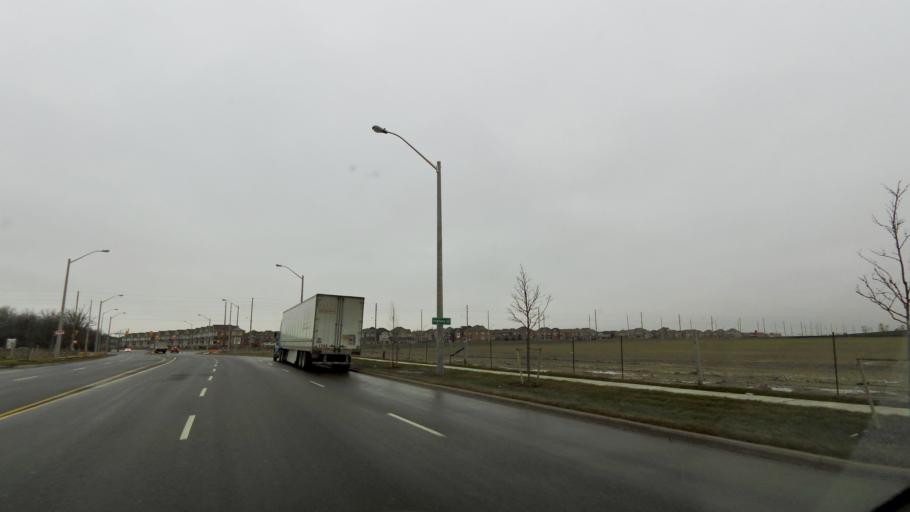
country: CA
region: Ontario
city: Brampton
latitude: 43.7928
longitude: -79.6605
